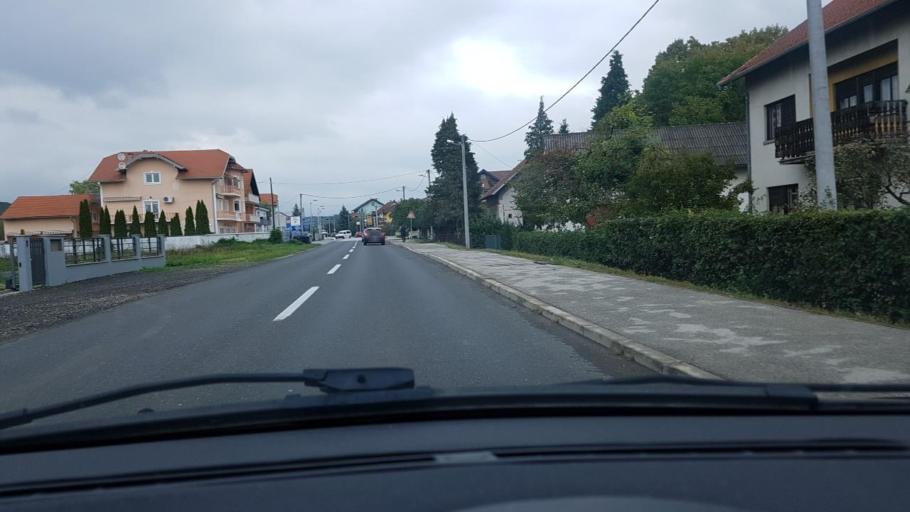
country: HR
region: Grad Zagreb
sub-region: Sesvete
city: Sesvete
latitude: 45.8525
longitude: 16.1121
